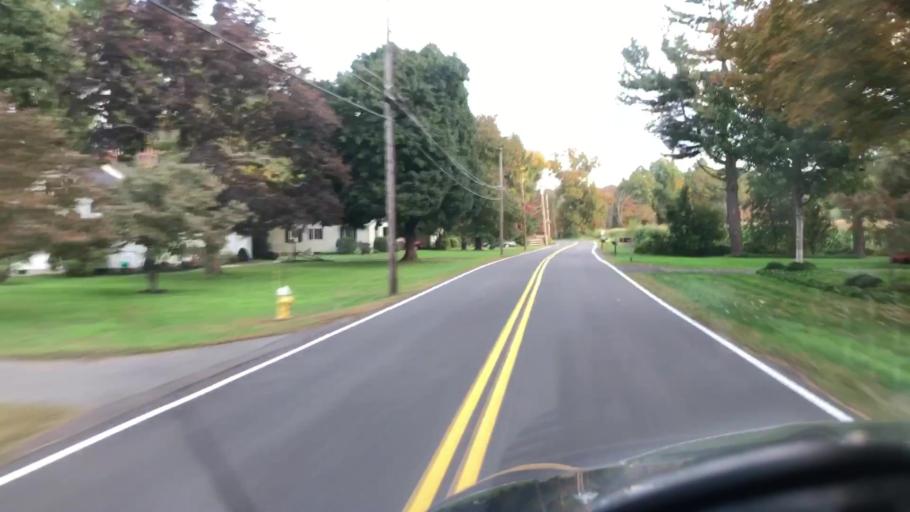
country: US
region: Connecticut
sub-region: Hartford County
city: Suffield Depot
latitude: 42.0177
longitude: -72.6575
